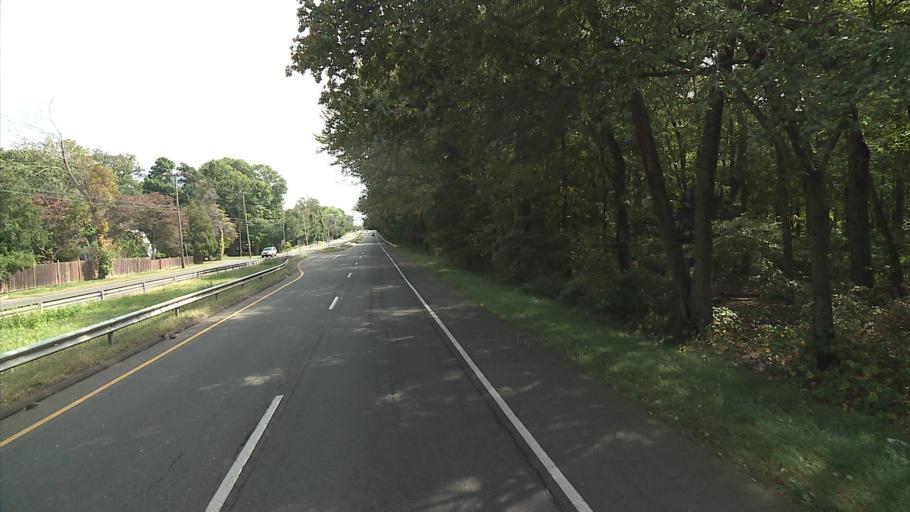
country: US
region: Connecticut
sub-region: New Haven County
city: Orange
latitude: 41.2989
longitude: -73.0107
